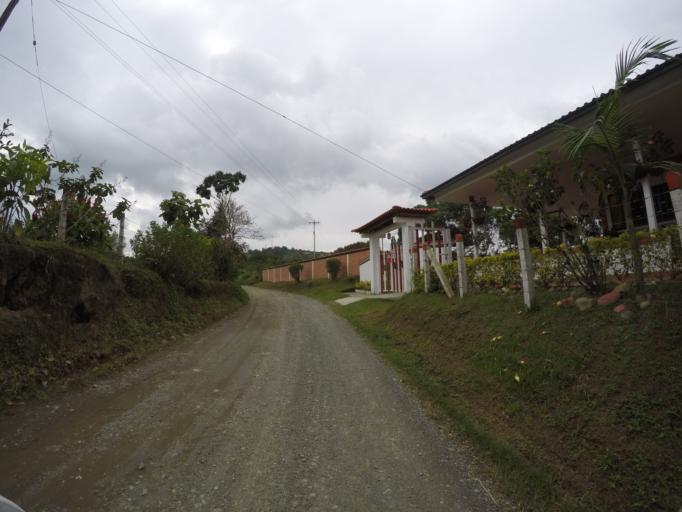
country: CO
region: Quindio
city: Filandia
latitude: 4.6463
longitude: -75.6755
